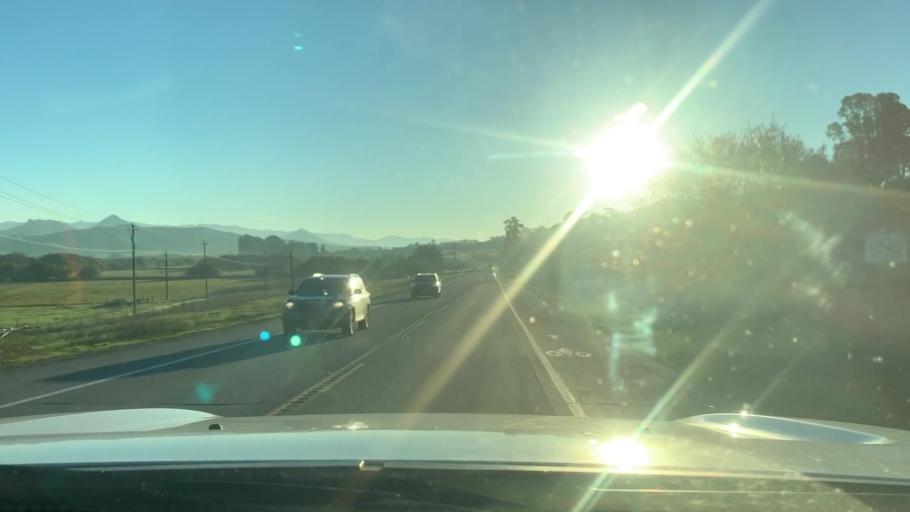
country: US
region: California
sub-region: San Luis Obispo County
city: Los Osos
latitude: 35.3016
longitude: -120.7930
